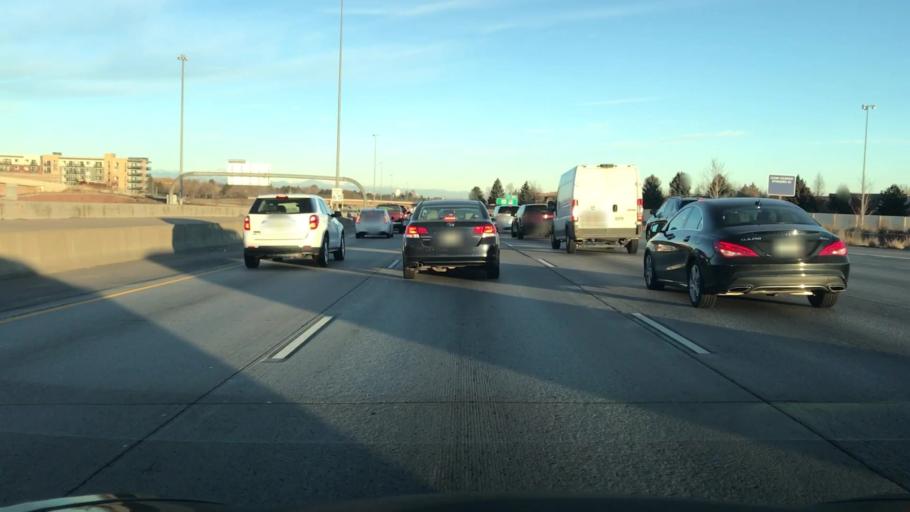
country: US
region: Colorado
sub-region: Arapahoe County
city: Greenwood Village
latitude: 39.6350
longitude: -104.9090
